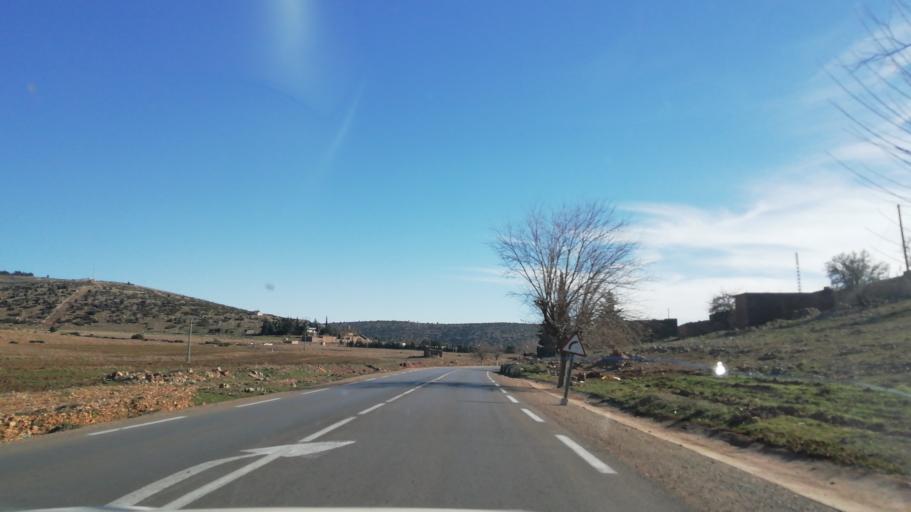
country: DZ
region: Tlemcen
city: Sebdou
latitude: 34.7096
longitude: -1.3212
